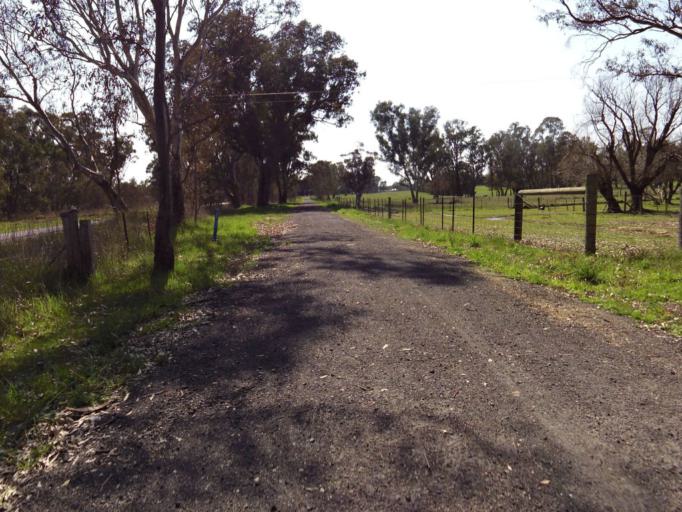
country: AU
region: Victoria
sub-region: Murrindindi
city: Alexandra
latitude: -37.1156
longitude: 145.6064
